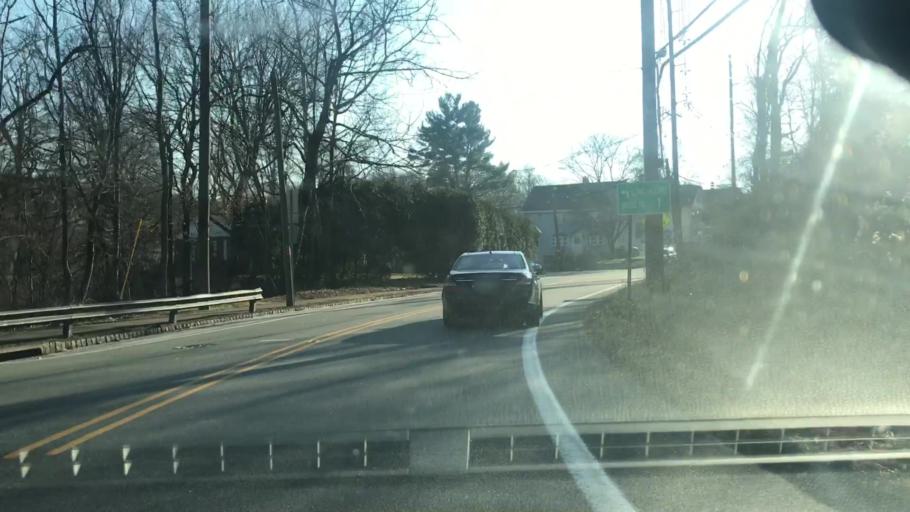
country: US
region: New Jersey
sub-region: Passaic County
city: Little Falls
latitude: 40.8720
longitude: -74.2063
